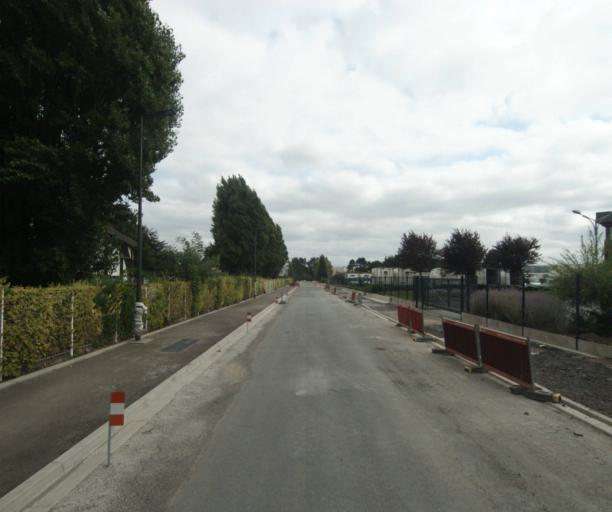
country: FR
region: Nord-Pas-de-Calais
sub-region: Departement du Nord
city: Toufflers
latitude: 50.6709
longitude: 3.2319
